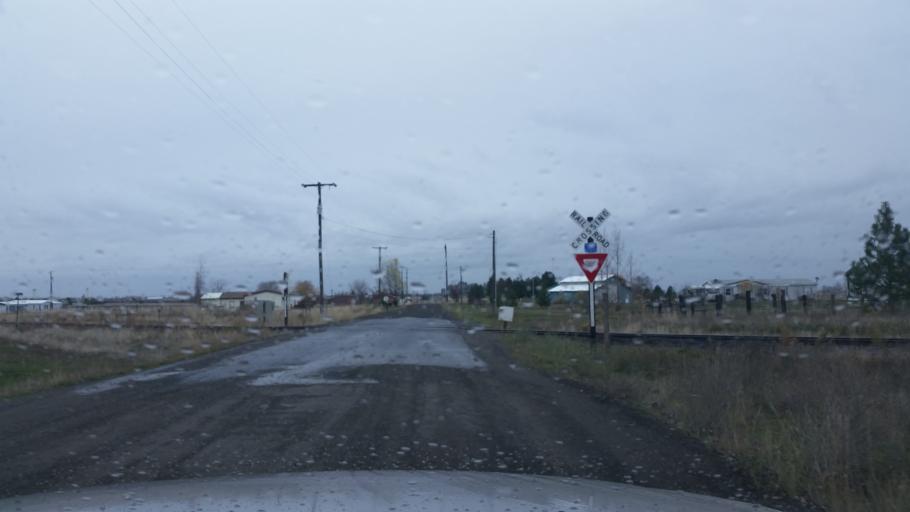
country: US
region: Washington
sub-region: Spokane County
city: Fairchild Air Force Base
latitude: 47.5854
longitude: -117.6289
